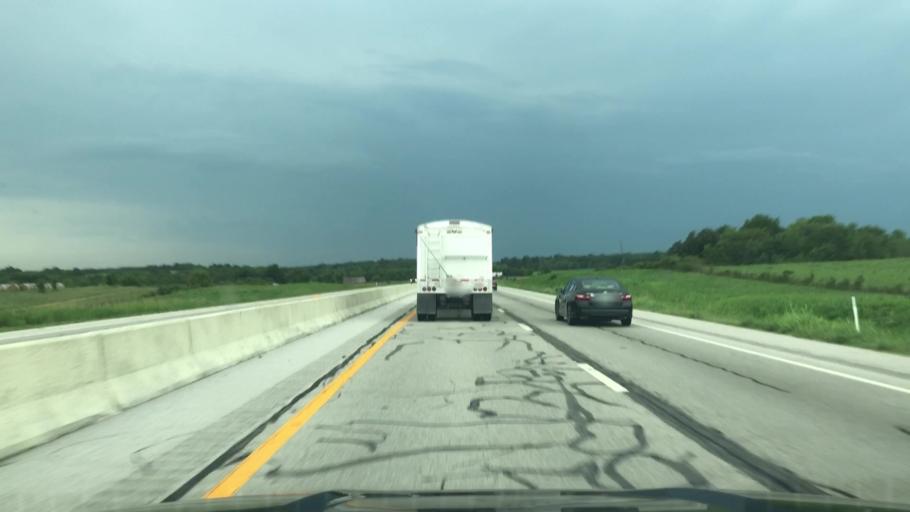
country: US
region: Oklahoma
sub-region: Rogers County
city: Bushyhead
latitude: 36.4063
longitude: -95.4108
